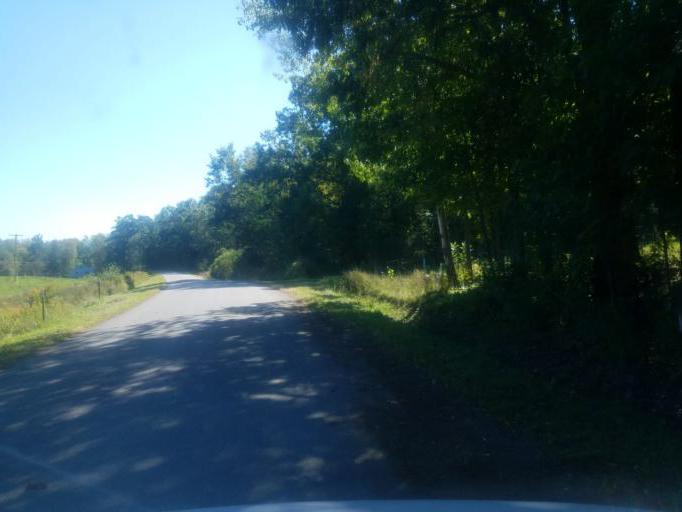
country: US
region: New York
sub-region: Allegany County
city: Houghton
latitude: 42.3150
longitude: -78.2066
